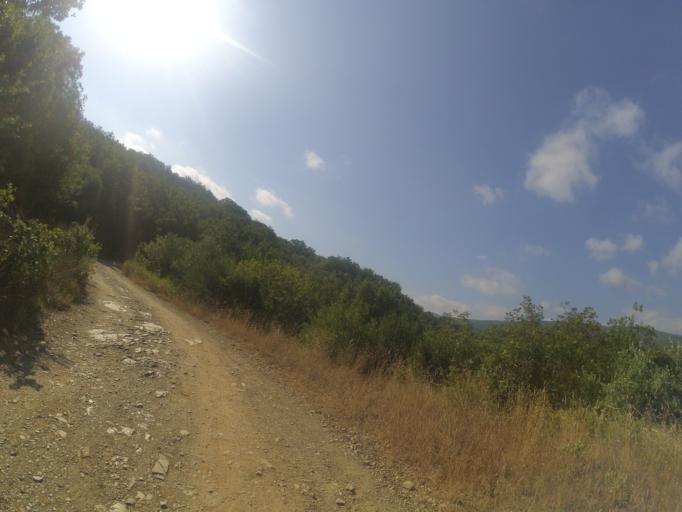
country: FR
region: Languedoc-Roussillon
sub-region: Departement des Pyrenees-Orientales
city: Ille-sur-Tet
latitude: 42.6482
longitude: 2.6272
